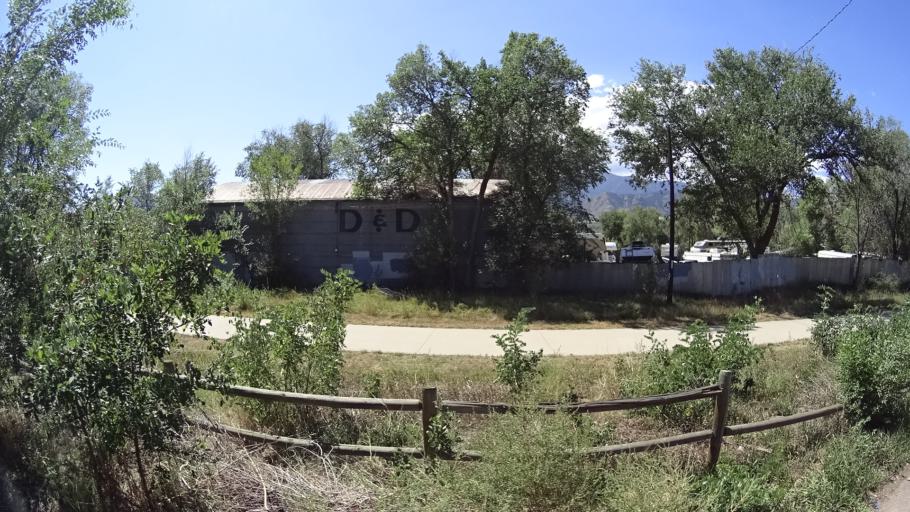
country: US
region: Colorado
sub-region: El Paso County
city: Colorado Springs
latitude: 38.8391
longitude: -104.8542
